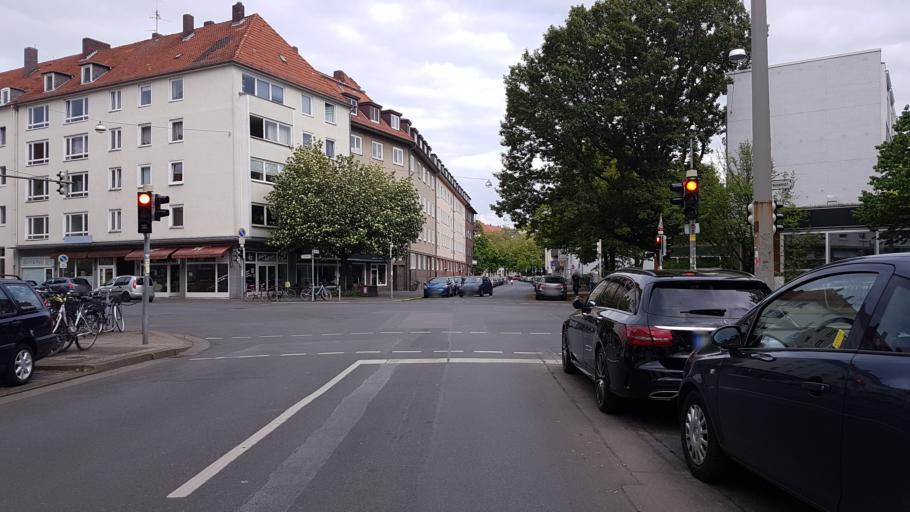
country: DE
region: Lower Saxony
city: Hannover
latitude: 52.3631
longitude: 9.7520
